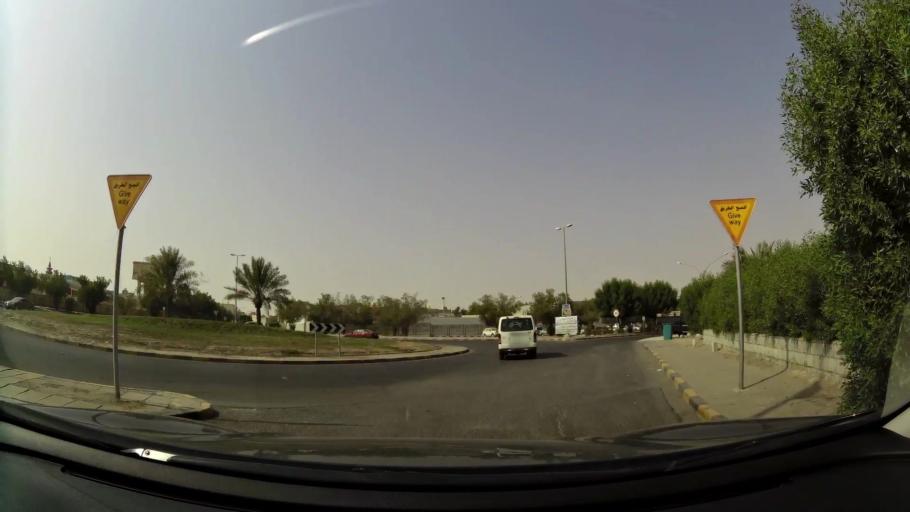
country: KW
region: Muhafazat al Jahra'
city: Al Jahra'
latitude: 29.3239
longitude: 47.6549
